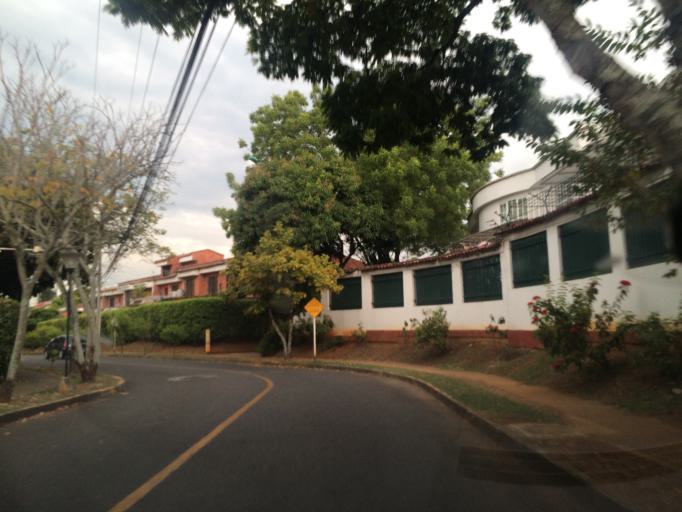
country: CO
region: Valle del Cauca
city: Cali
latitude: 3.3694
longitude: -76.5387
